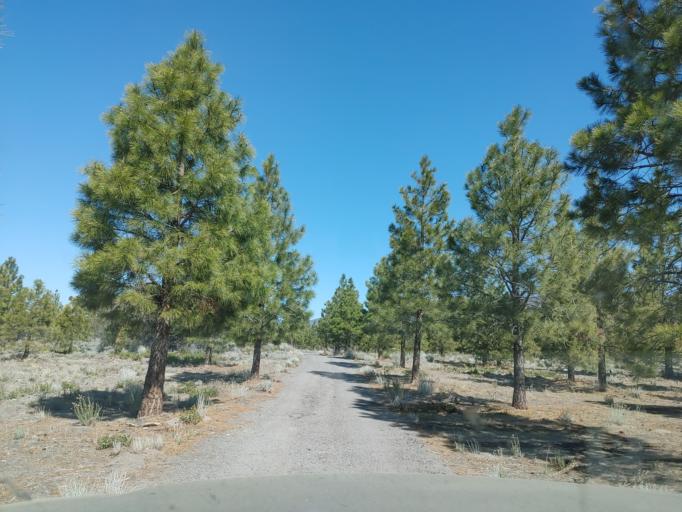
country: US
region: California
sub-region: Siskiyou County
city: Weed
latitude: 41.5439
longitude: -122.2320
